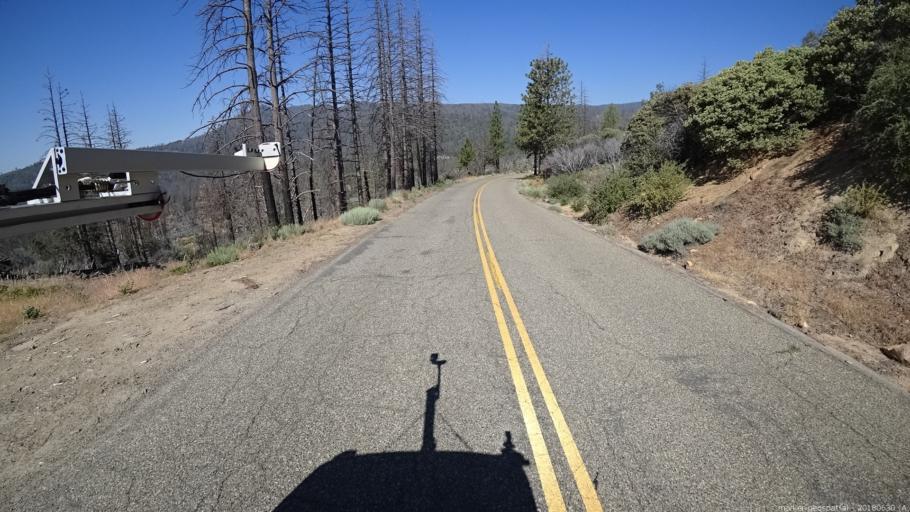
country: US
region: California
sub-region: Fresno County
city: Auberry
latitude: 37.2466
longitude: -119.3497
